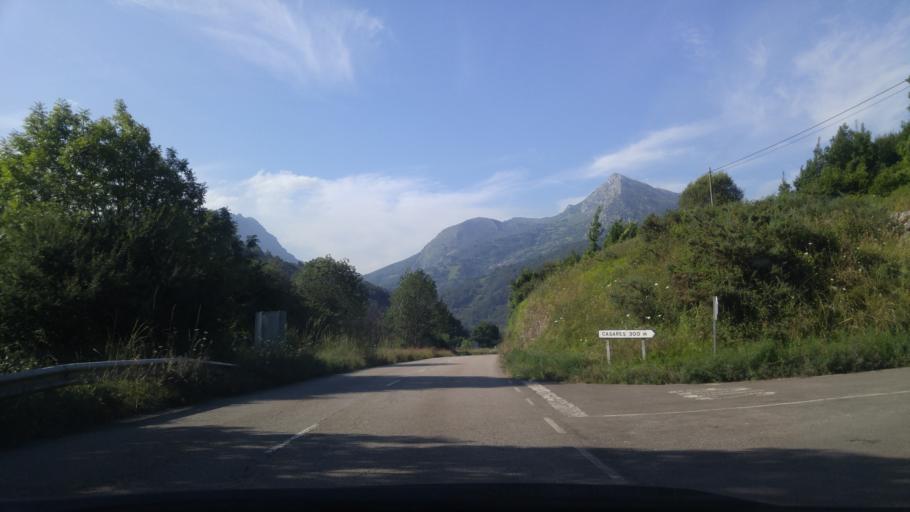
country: ES
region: Asturias
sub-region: Province of Asturias
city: Barzana
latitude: 43.1791
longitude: -5.9939
